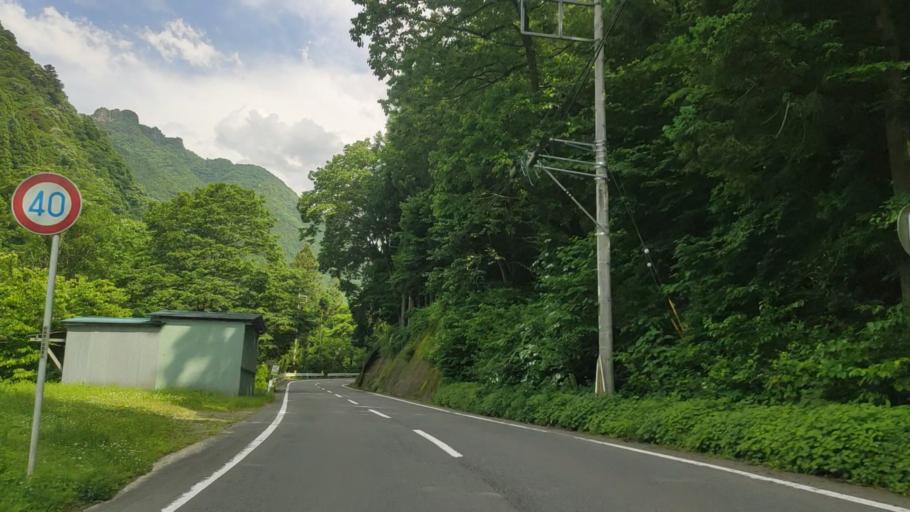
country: JP
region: Gunma
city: Tomioka
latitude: 36.1503
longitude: 138.7310
